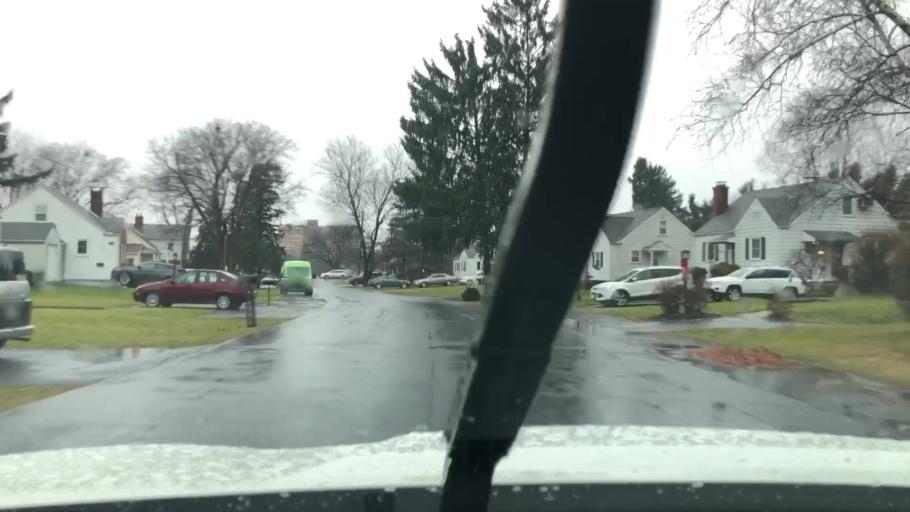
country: US
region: Pennsylvania
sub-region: Northampton County
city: Bethlehem
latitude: 40.6451
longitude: -75.4030
